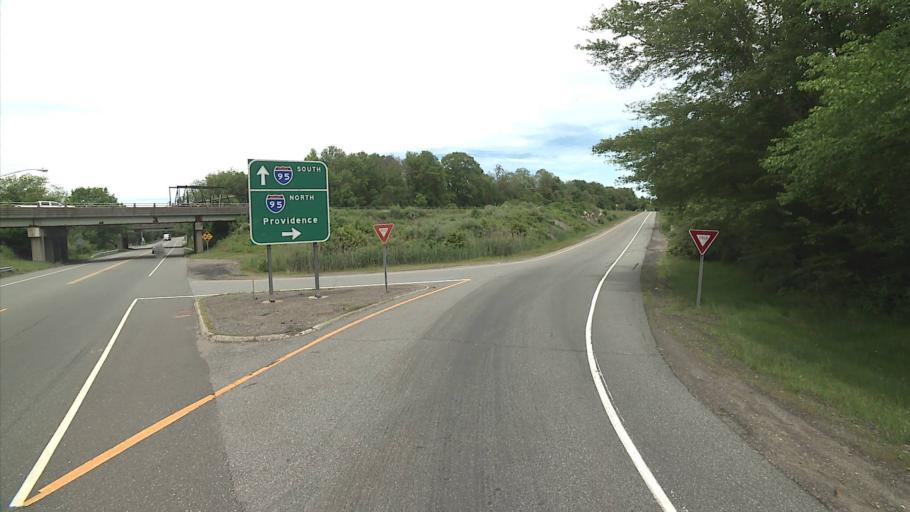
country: US
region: Connecticut
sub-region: New London County
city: Old Mystic
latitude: 41.3780
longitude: -71.9044
